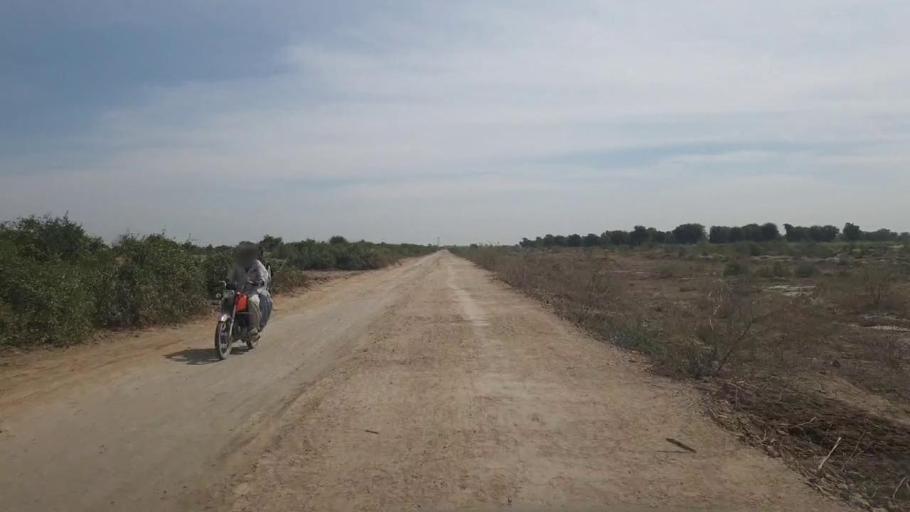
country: PK
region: Sindh
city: Kunri
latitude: 25.2971
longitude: 69.5790
